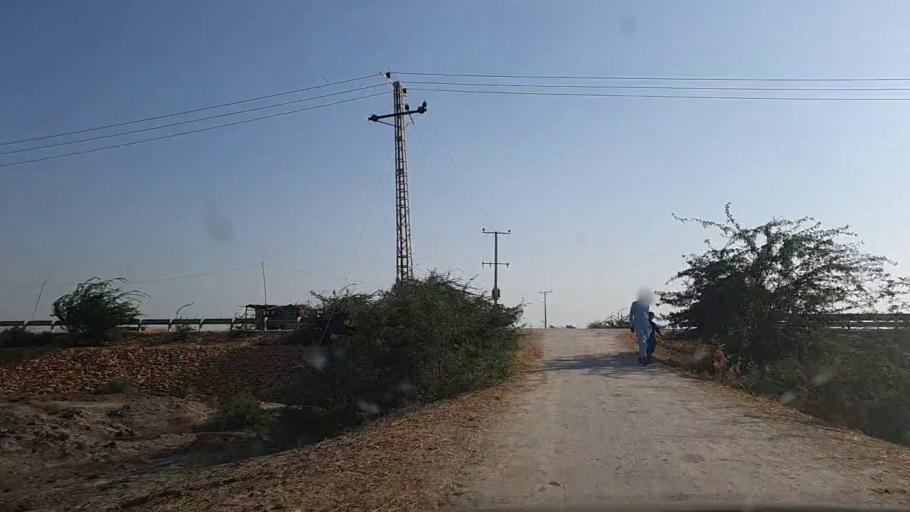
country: PK
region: Sindh
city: Thatta
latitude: 24.6189
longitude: 68.0780
